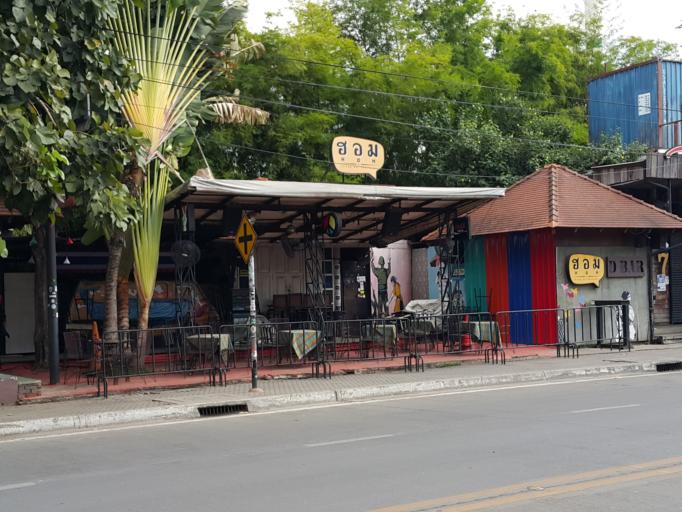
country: TH
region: Chiang Mai
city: Chiang Mai
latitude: 18.8069
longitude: 98.9952
